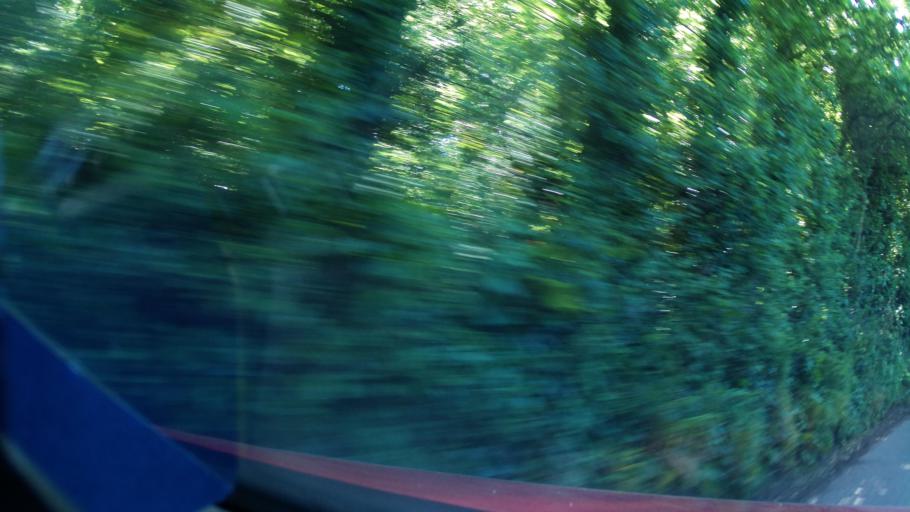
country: GB
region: England
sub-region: Devon
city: Exmouth
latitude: 50.6168
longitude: -3.3812
